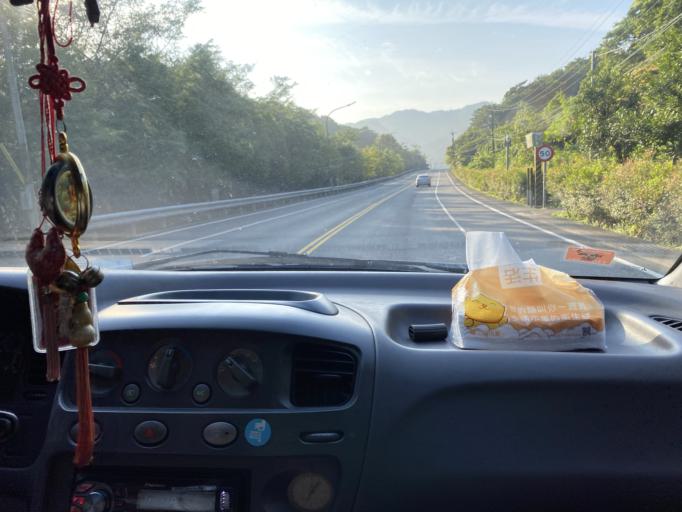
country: TW
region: Taiwan
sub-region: Keelung
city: Keelung
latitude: 25.0508
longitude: 121.7748
